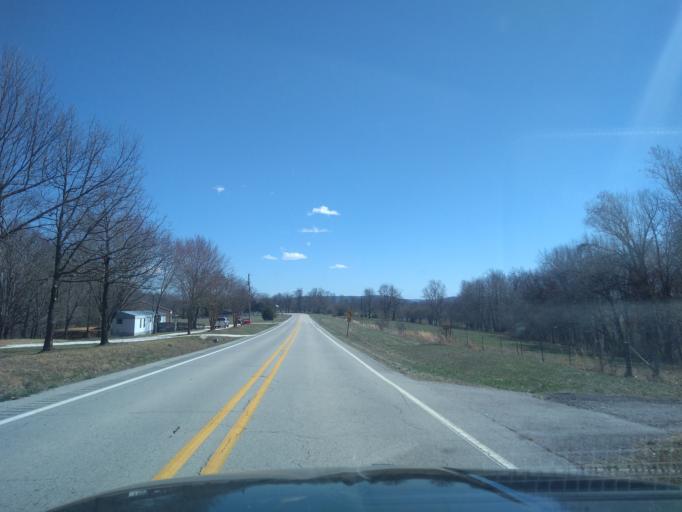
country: US
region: Arkansas
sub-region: Washington County
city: Farmington
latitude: 36.0813
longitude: -94.3109
